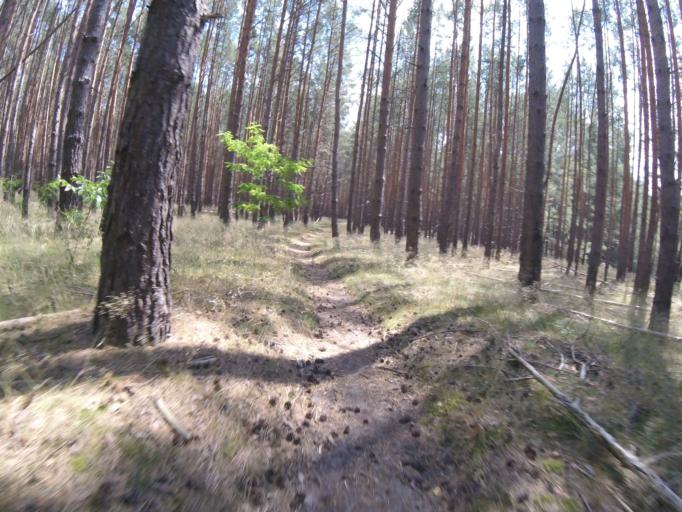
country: DE
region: Brandenburg
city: Bestensee
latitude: 52.2715
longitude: 13.6920
